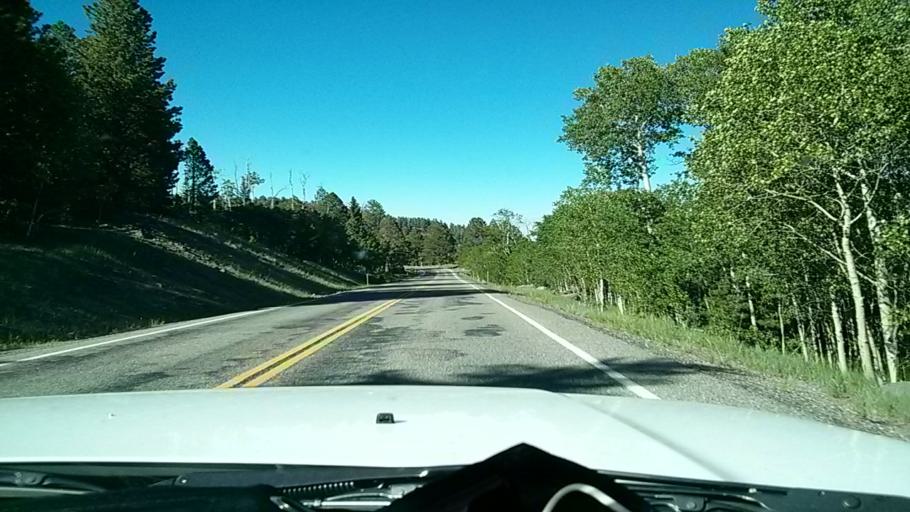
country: US
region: Utah
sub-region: Wayne County
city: Loa
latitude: 38.0817
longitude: -111.3389
